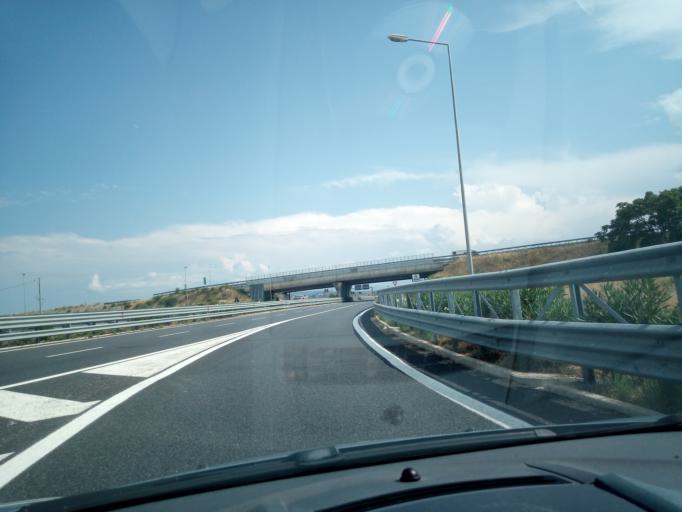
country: IT
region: Calabria
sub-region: Provincia di Cosenza
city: Firmo
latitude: 39.7225
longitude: 16.2384
